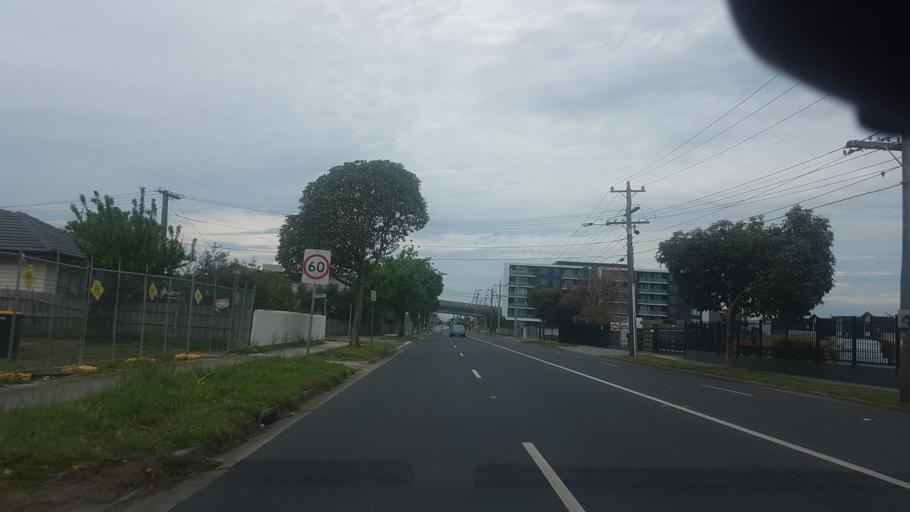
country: AU
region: Victoria
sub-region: Kingston
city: Clayton South
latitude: -37.9287
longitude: 145.1244
